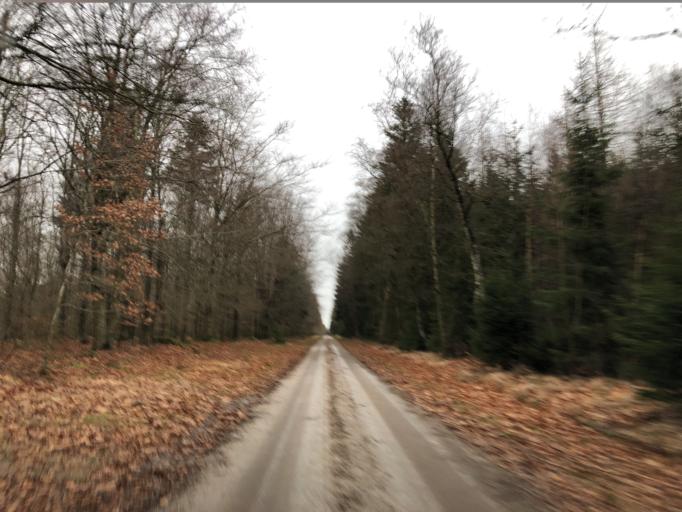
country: DK
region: Central Jutland
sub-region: Holstebro Kommune
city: Vinderup
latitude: 56.3834
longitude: 8.8664
